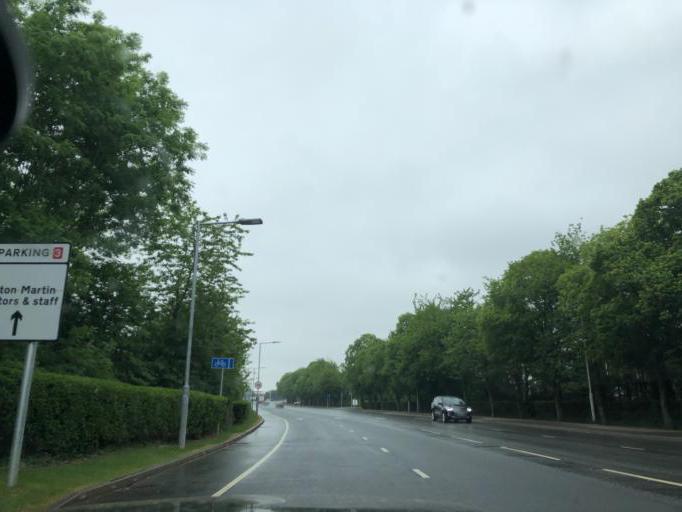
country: GB
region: England
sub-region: Warwickshire
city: Harbury
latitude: 52.1971
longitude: -1.4827
